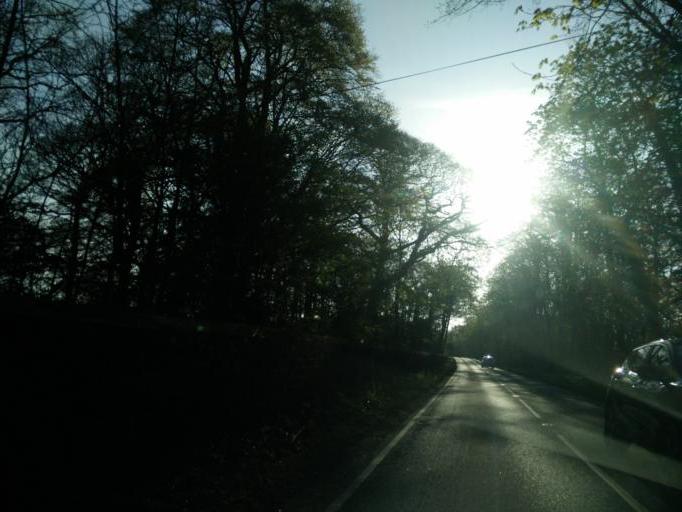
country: GB
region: England
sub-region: Stockton-on-Tees
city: Grindon
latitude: 54.6159
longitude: -1.3504
